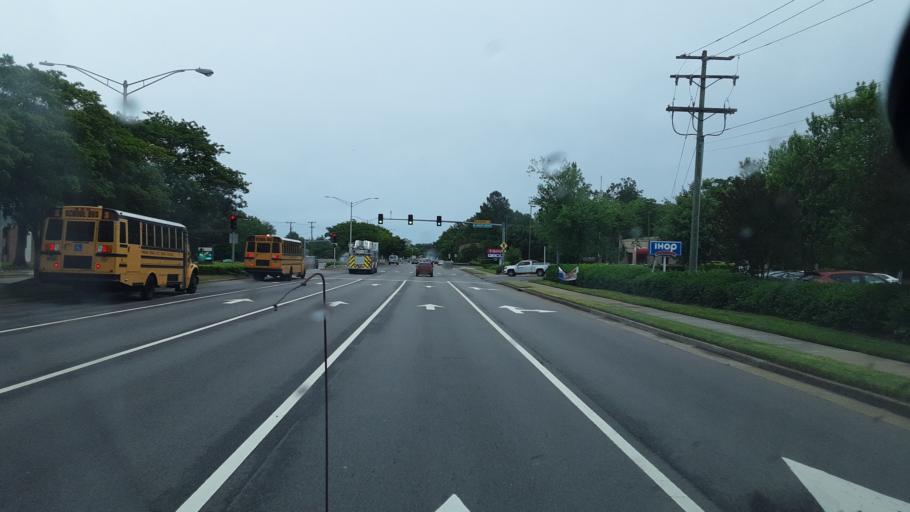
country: US
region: Virginia
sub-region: City of Chesapeake
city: Chesapeake
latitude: 36.8433
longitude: -76.1275
